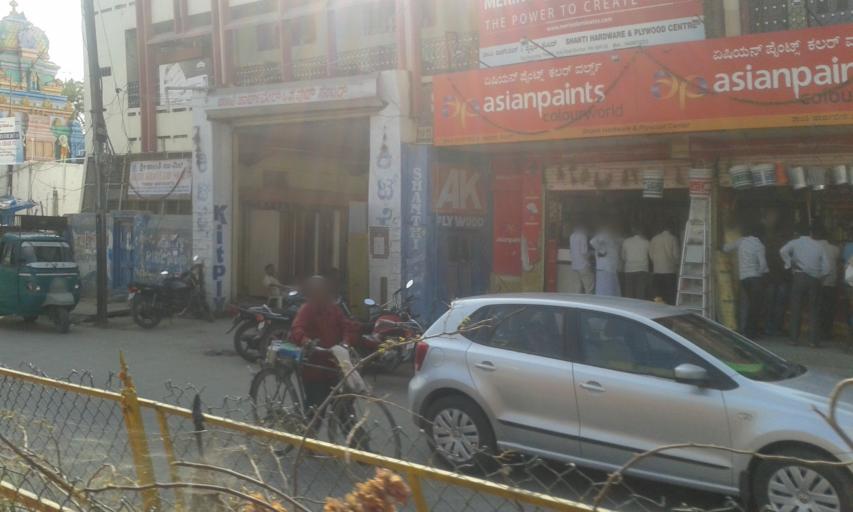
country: IN
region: Karnataka
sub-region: Raichur
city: Raichur
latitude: 16.2125
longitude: 77.3571
